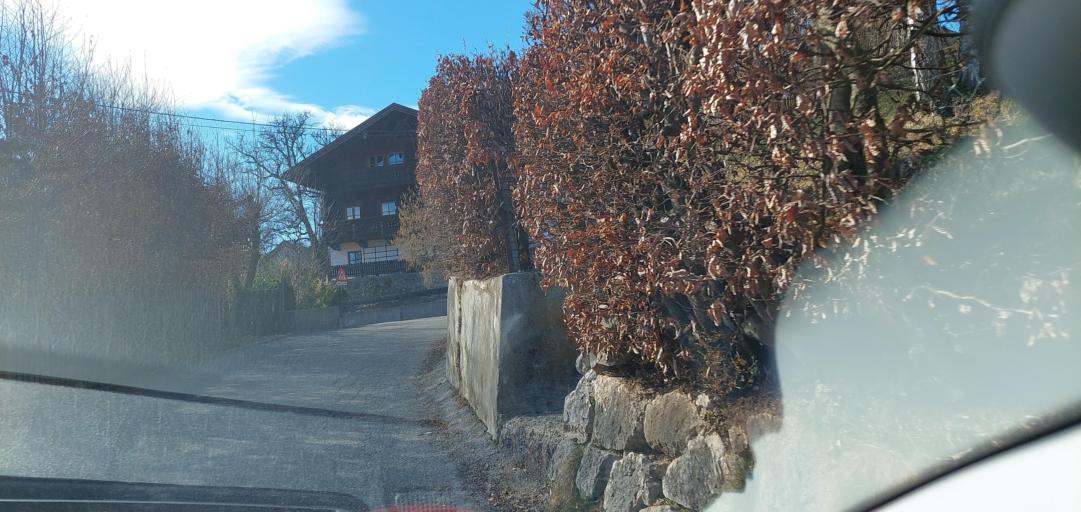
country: AT
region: Upper Austria
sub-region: Politischer Bezirk Gmunden
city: Bad Ischl
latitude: 47.7098
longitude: 13.5997
